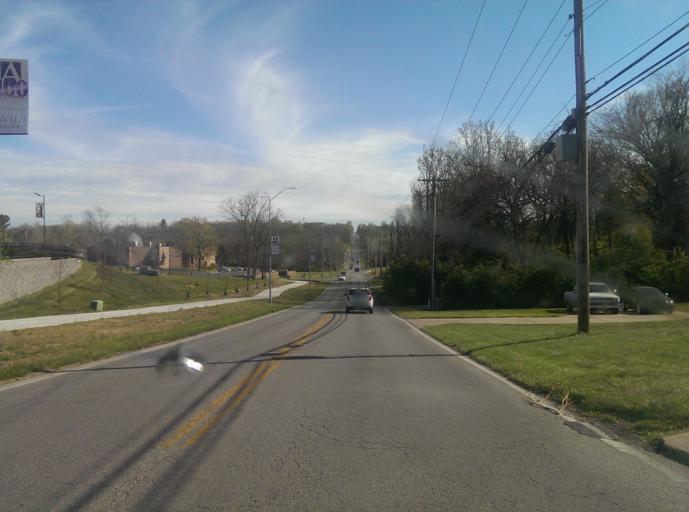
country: US
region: Kansas
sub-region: Johnson County
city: Leawood
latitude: 38.9116
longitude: -94.5937
